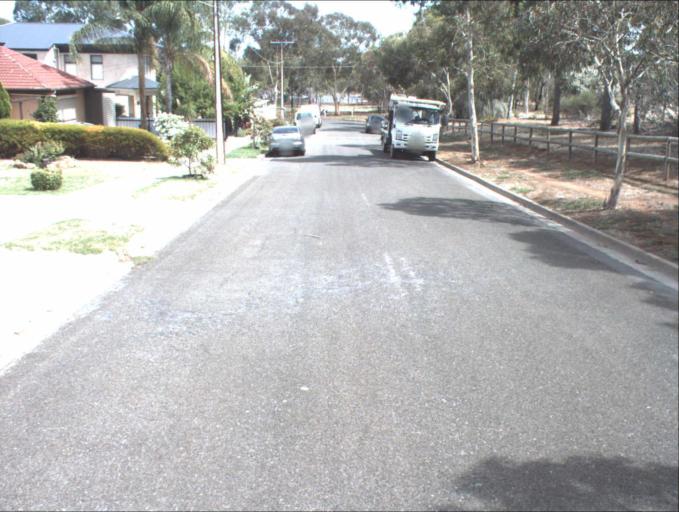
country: AU
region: South Australia
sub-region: Port Adelaide Enfield
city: Enfield
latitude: -34.8463
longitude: 138.6097
